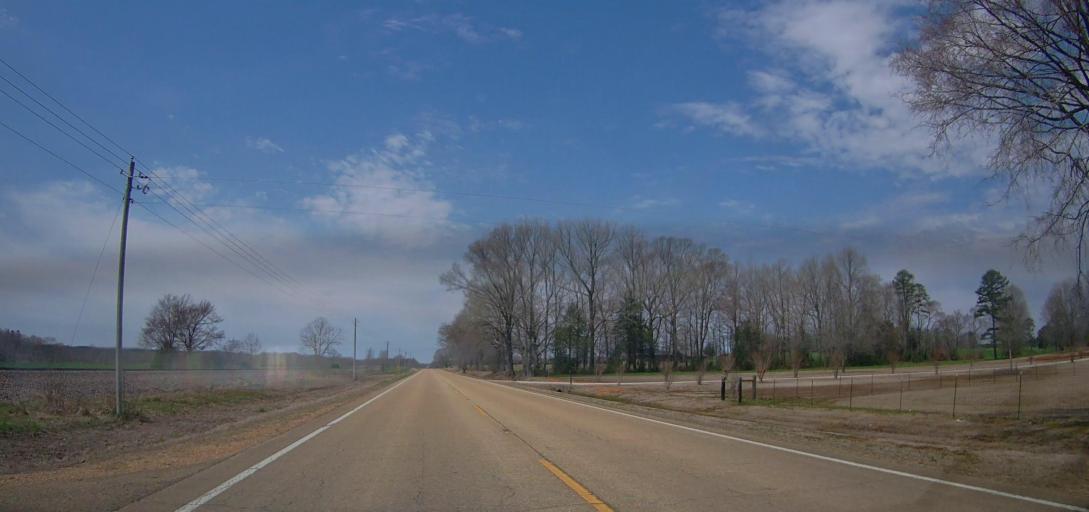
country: US
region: Mississippi
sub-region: Benton County
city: Ashland
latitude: 34.6198
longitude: -89.2262
